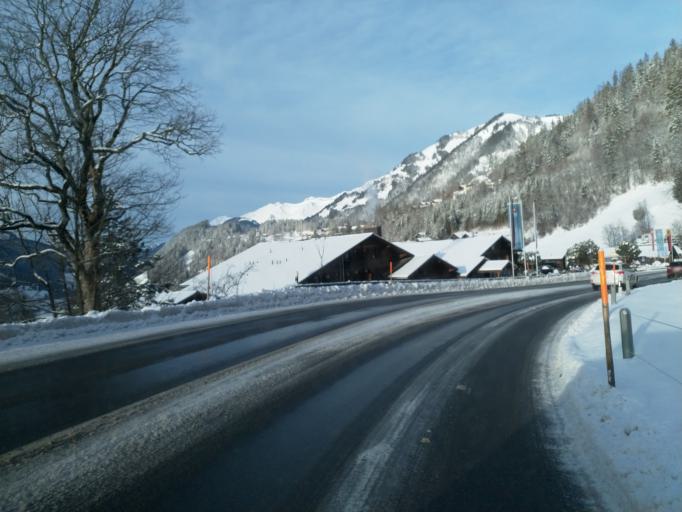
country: CH
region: Bern
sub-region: Obersimmental-Saanen District
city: Saanen
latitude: 46.4930
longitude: 7.2679
